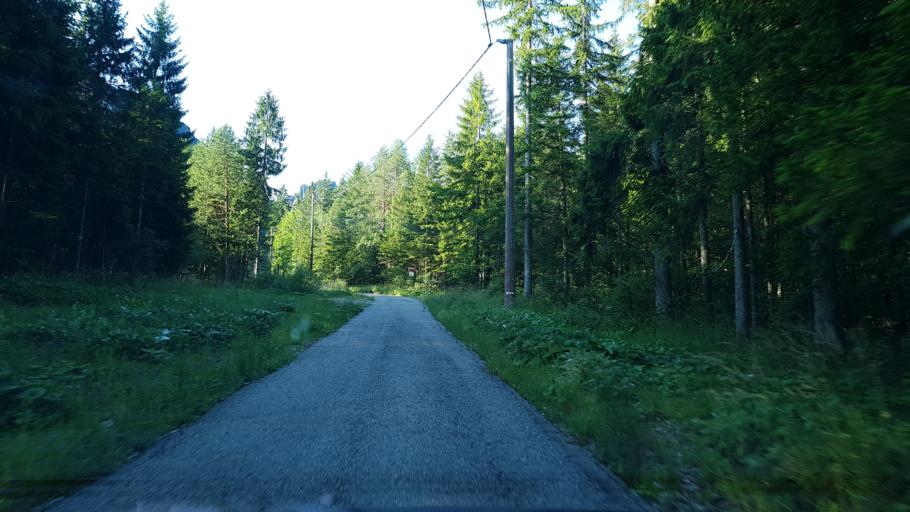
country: IT
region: Friuli Venezia Giulia
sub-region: Provincia di Udine
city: Pontebba
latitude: 46.5028
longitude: 13.2532
